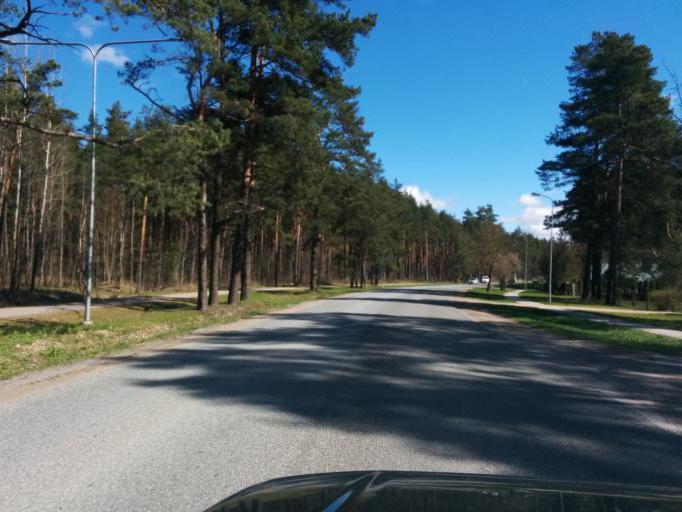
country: LV
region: Kekava
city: Balozi
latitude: 56.8792
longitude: 24.1269
